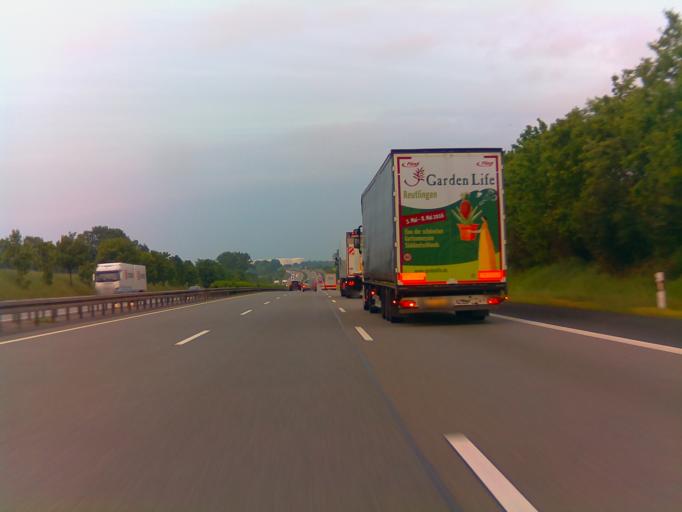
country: DE
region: Thuringia
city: Emleben
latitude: 50.9067
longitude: 10.6656
